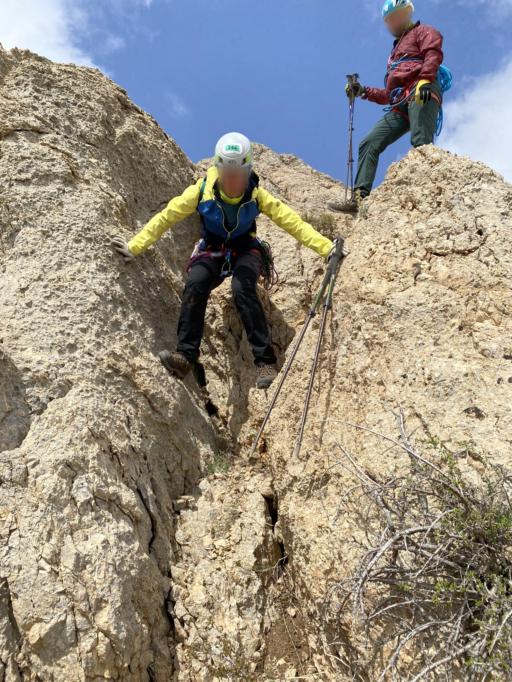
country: KZ
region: Ongtustik Qazaqstan
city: Ashchysay
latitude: 43.7439
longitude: 68.8381
